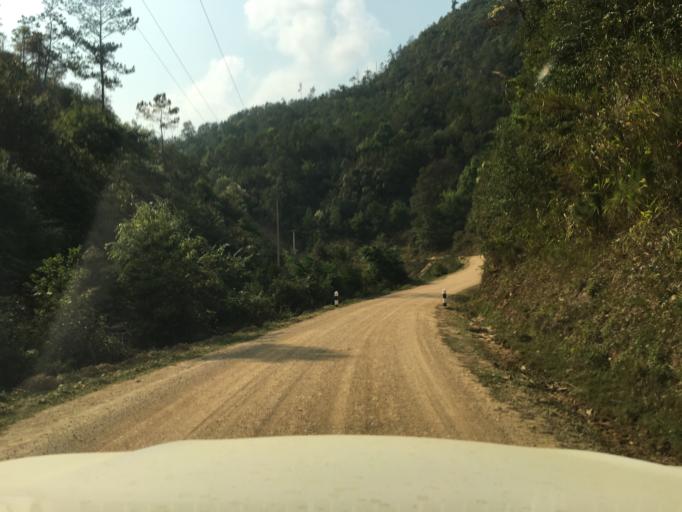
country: LA
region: Houaphan
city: Huameung
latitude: 20.2028
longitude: 103.8446
